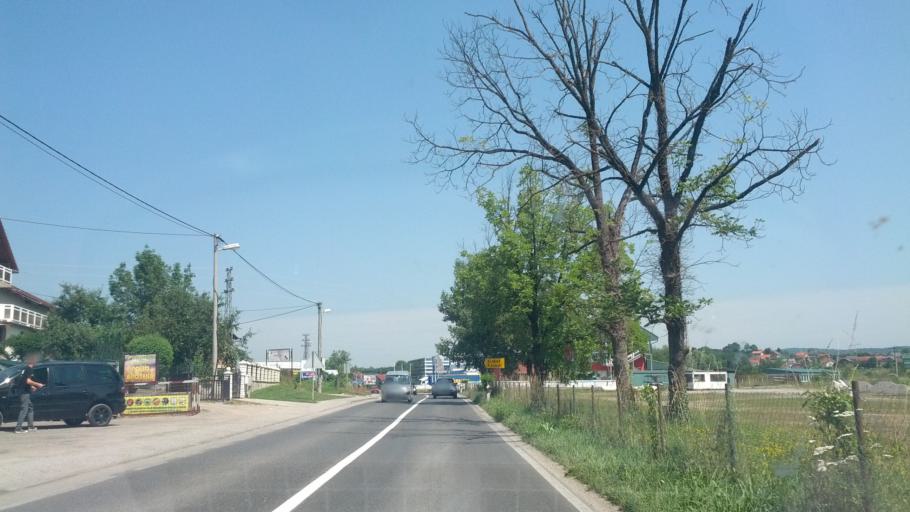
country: BA
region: Federation of Bosnia and Herzegovina
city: Bihac
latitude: 44.8332
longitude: 15.8323
